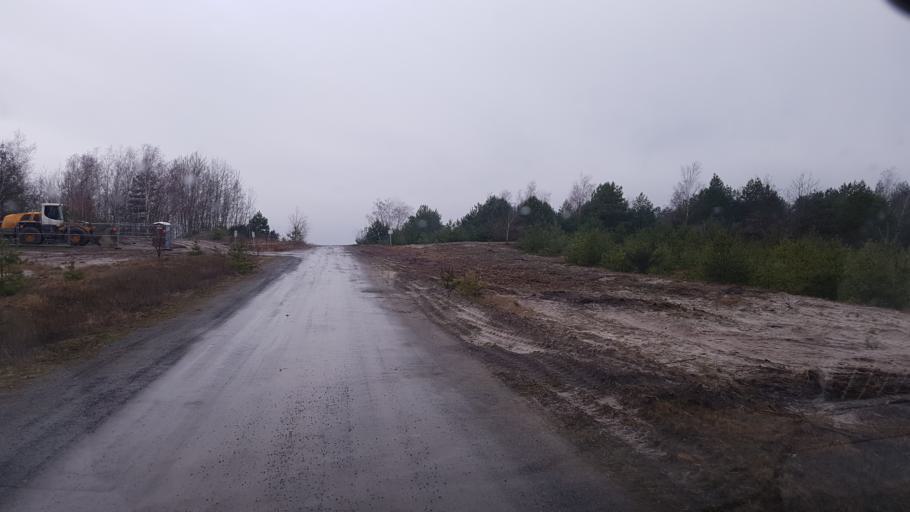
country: DE
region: Brandenburg
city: Sallgast
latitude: 51.5770
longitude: 13.7716
